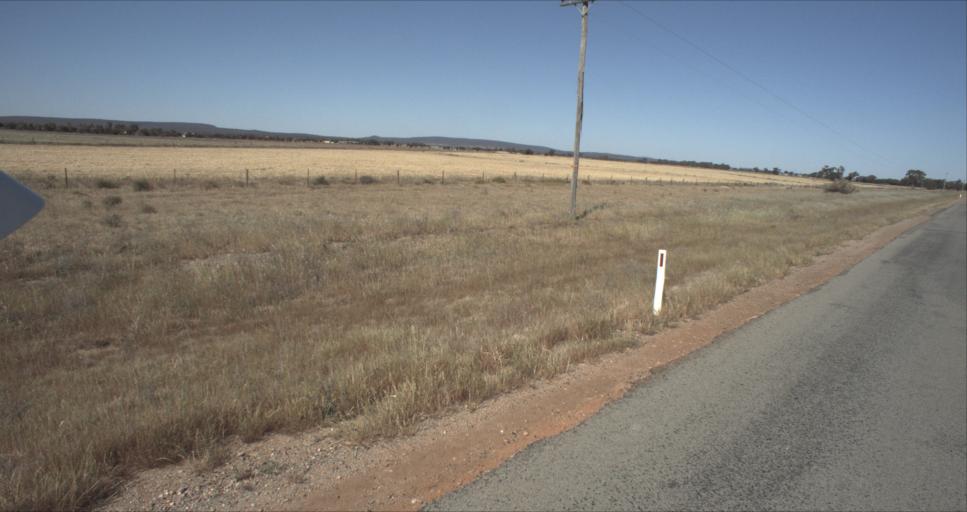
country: AU
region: New South Wales
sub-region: Leeton
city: Leeton
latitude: -34.4934
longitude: 146.3862
